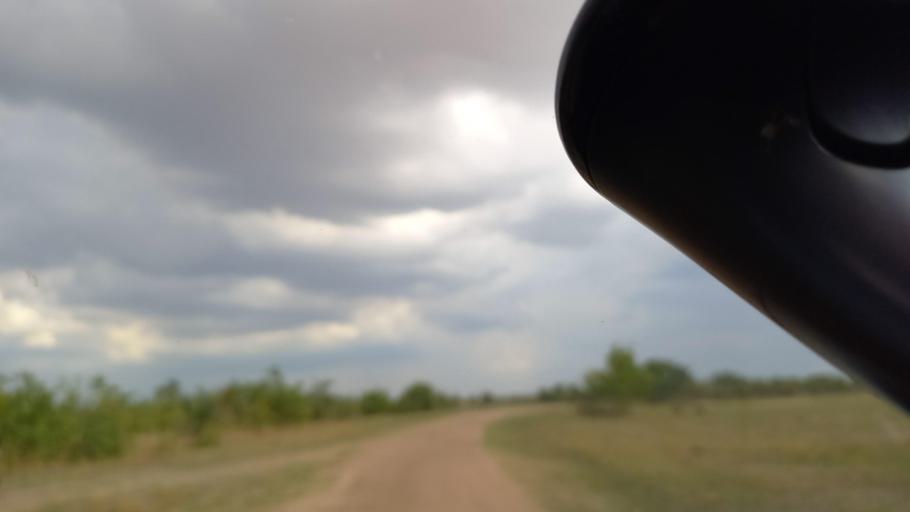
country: ZM
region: Lusaka
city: Kafue
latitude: -15.8382
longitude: 28.0866
